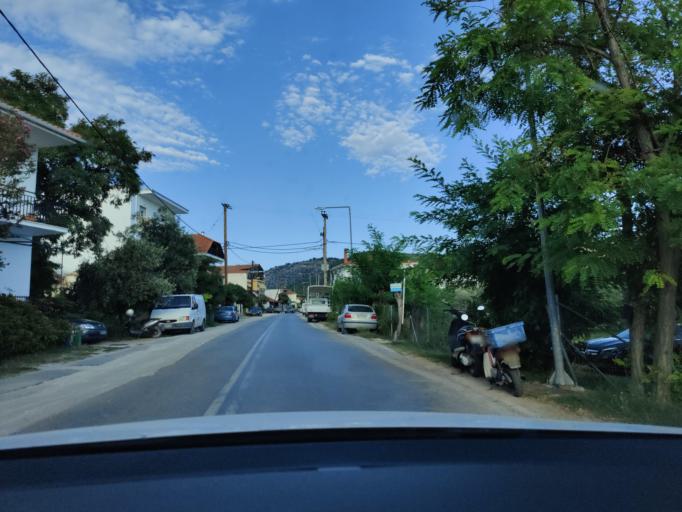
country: GR
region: East Macedonia and Thrace
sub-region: Nomos Kavalas
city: Limenaria
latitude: 40.6116
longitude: 24.6139
